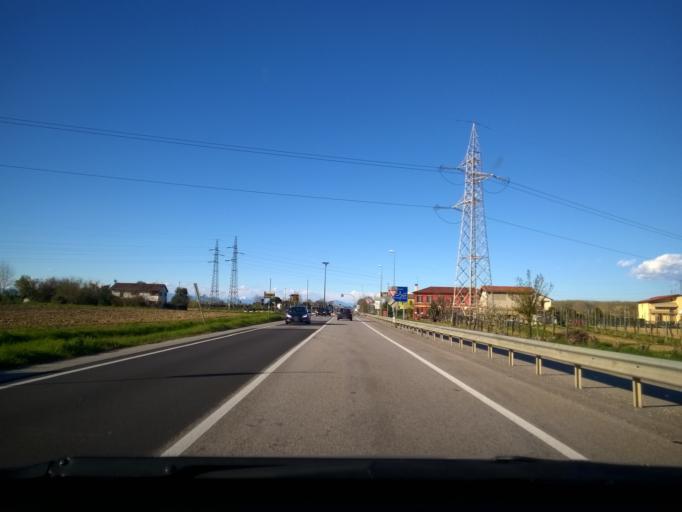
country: IT
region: Veneto
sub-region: Provincia di Venezia
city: Marano
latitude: 45.4676
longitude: 12.1084
